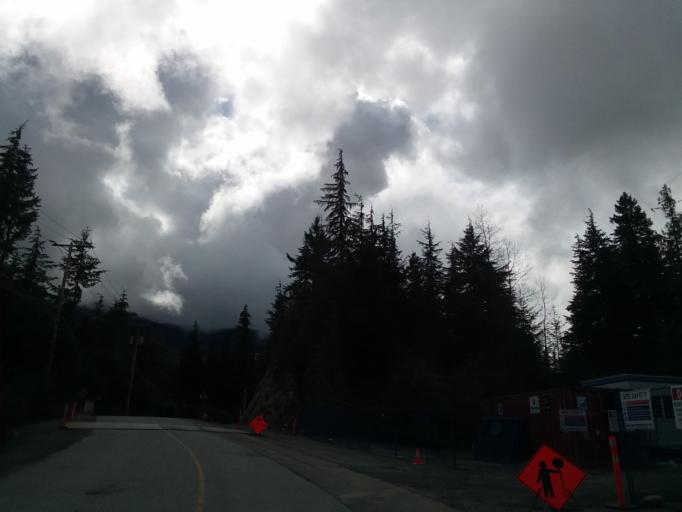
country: CA
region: British Columbia
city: Whistler
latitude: 50.0935
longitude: -123.0130
